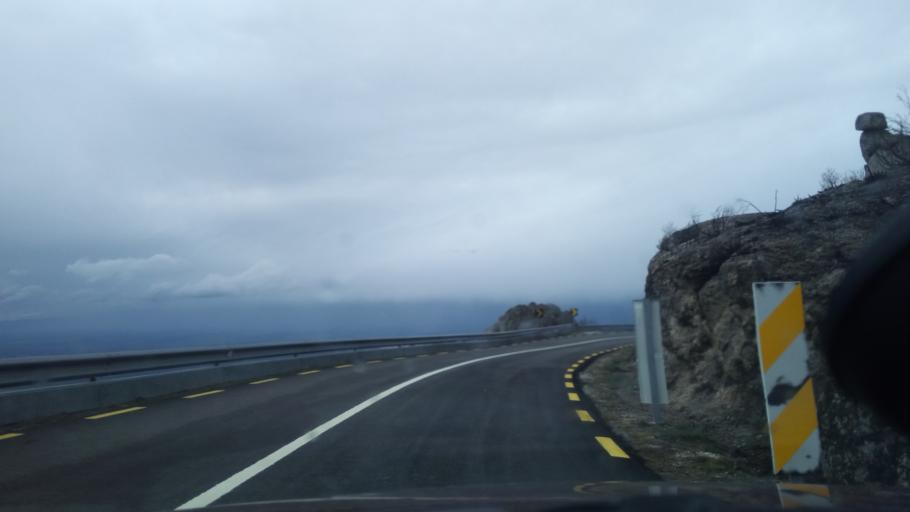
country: PT
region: Guarda
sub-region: Manteigas
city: Manteigas
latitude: 40.4337
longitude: -7.6042
